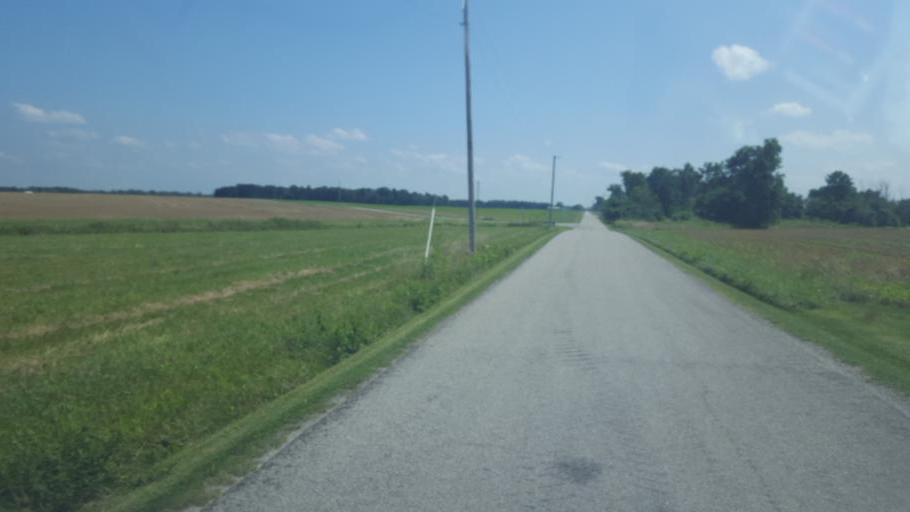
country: US
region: Ohio
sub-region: Huron County
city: Willard
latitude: 41.1435
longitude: -82.8151
